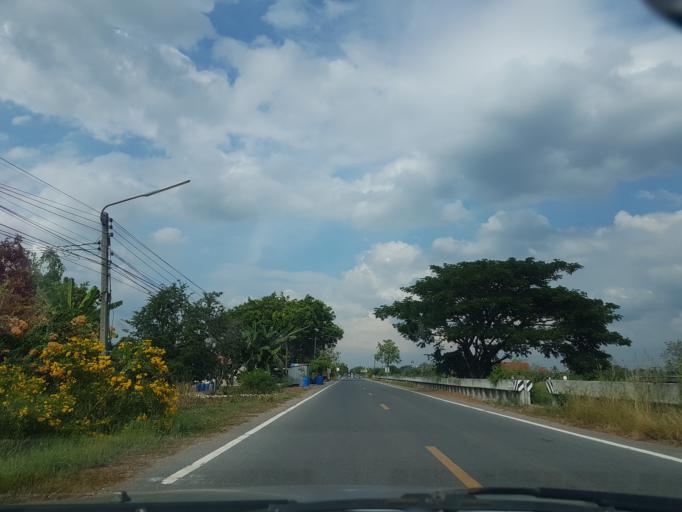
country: TH
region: Pathum Thani
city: Nong Suea
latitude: 14.1725
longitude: 100.8915
